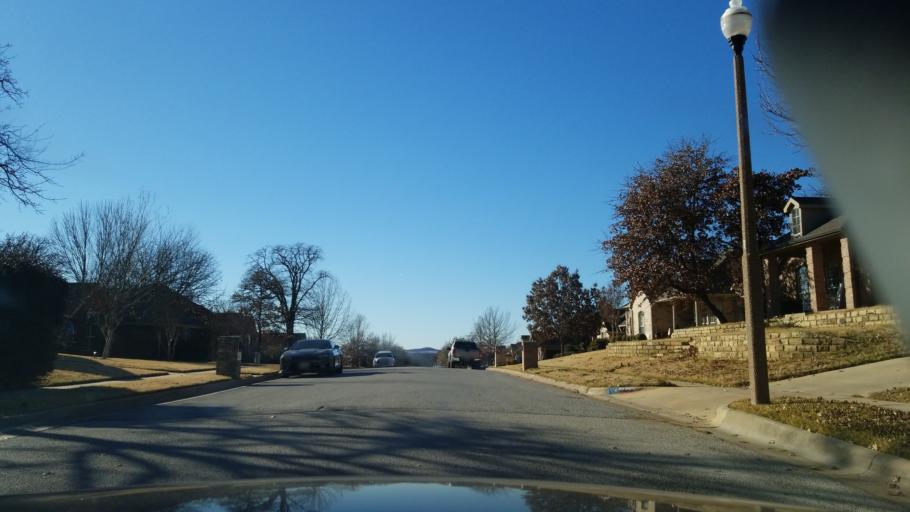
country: US
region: Texas
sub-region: Denton County
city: Corinth
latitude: 33.1503
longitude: -97.1162
